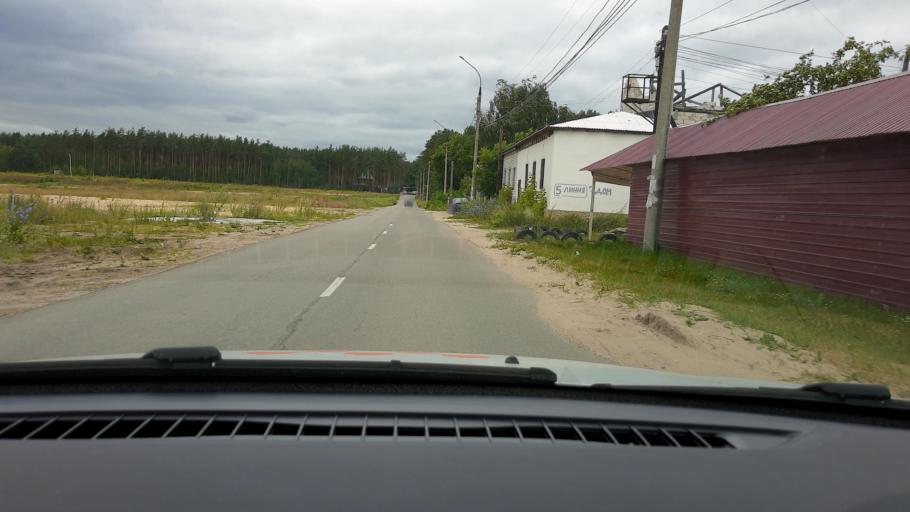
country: RU
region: Nizjnij Novgorod
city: Pyra
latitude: 56.2404
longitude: 43.3782
